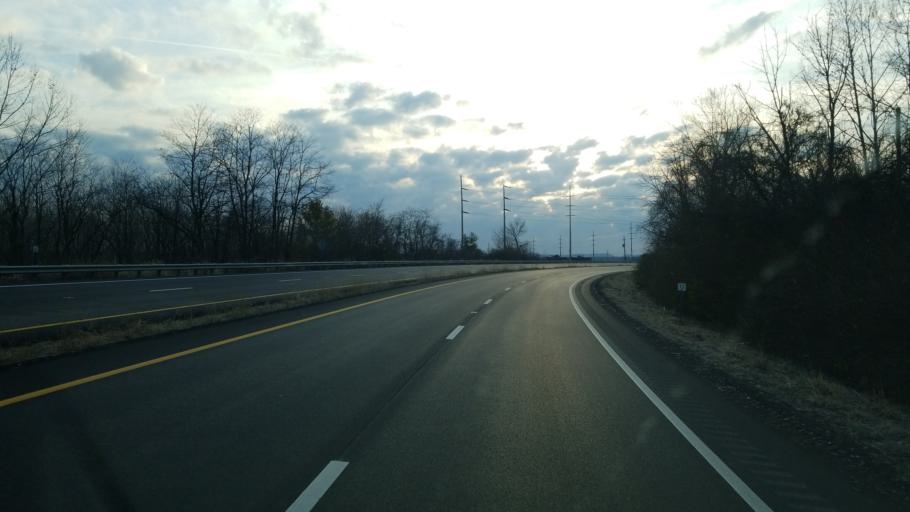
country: US
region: Ohio
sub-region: Ross County
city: Chillicothe
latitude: 39.3189
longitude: -82.9637
